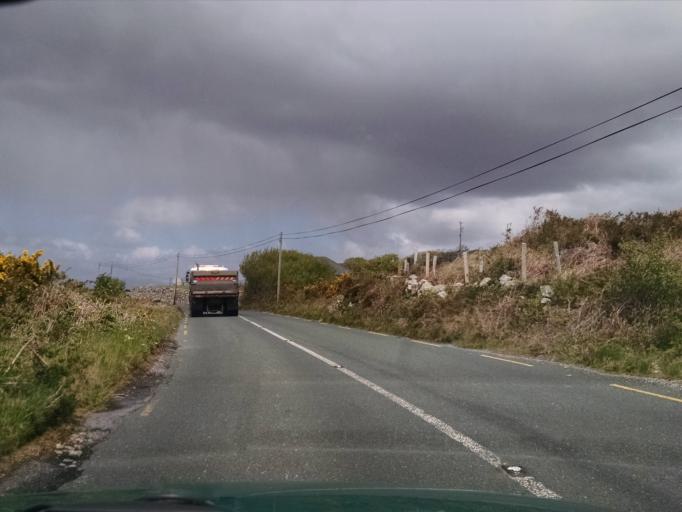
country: IE
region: Connaught
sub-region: County Galway
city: Oughterard
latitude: 53.3029
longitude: -9.5547
